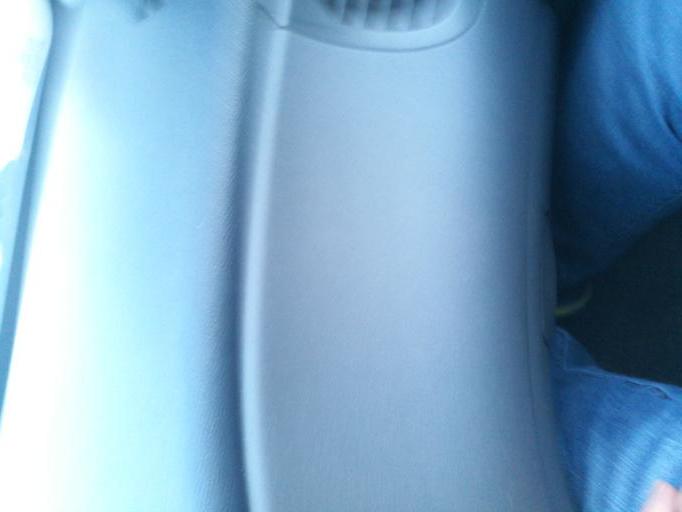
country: CL
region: O'Higgins
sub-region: Provincia de Cachapoal
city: Graneros
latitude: -34.0489
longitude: -70.7269
